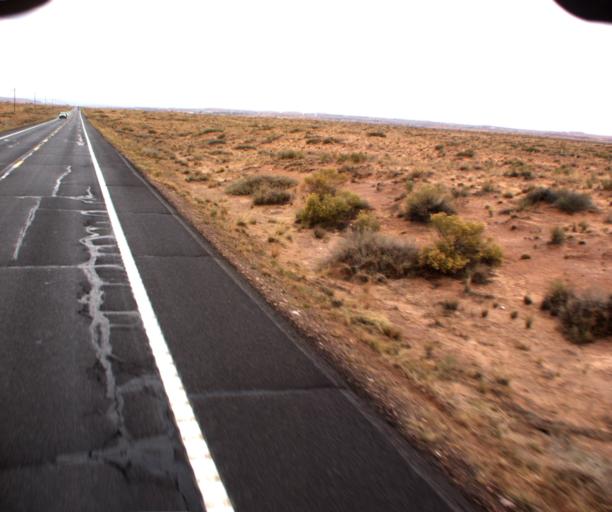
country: US
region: Arizona
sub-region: Coconino County
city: Tuba City
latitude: 36.1388
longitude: -111.1665
